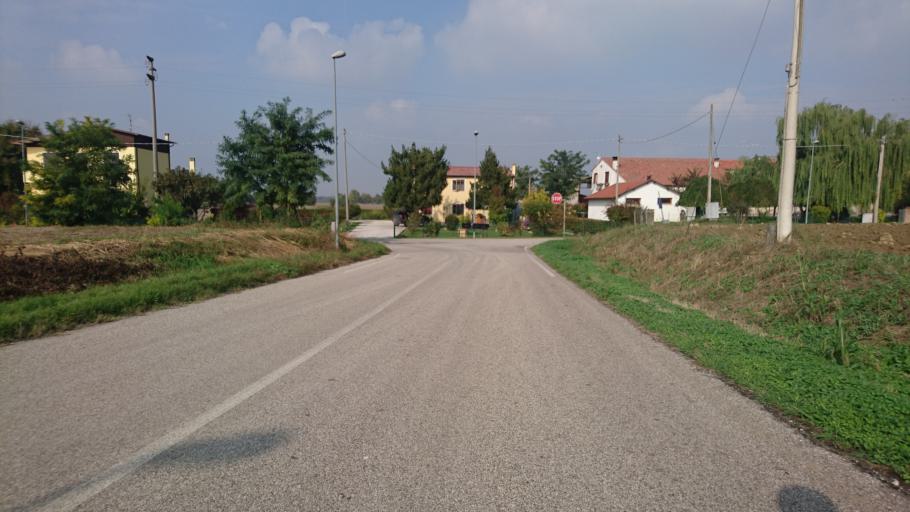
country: IT
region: Veneto
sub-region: Provincia di Rovigo
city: Grignano Polesine
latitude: 45.0443
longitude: 11.7662
